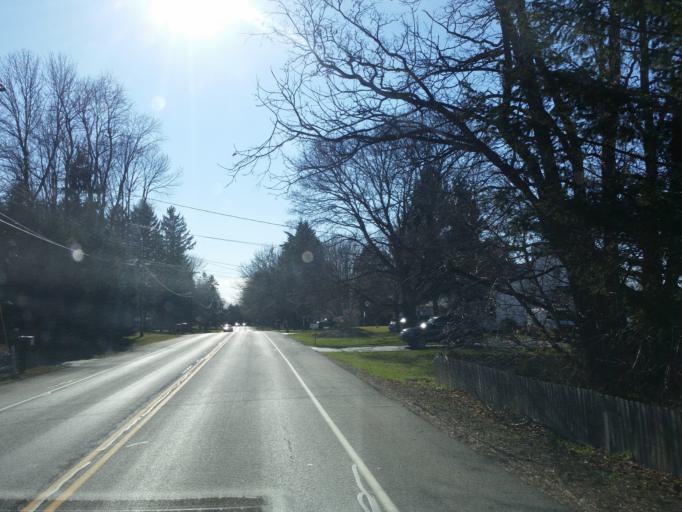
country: US
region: New York
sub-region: Monroe County
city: North Gates
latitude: 43.1141
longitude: -77.7561
